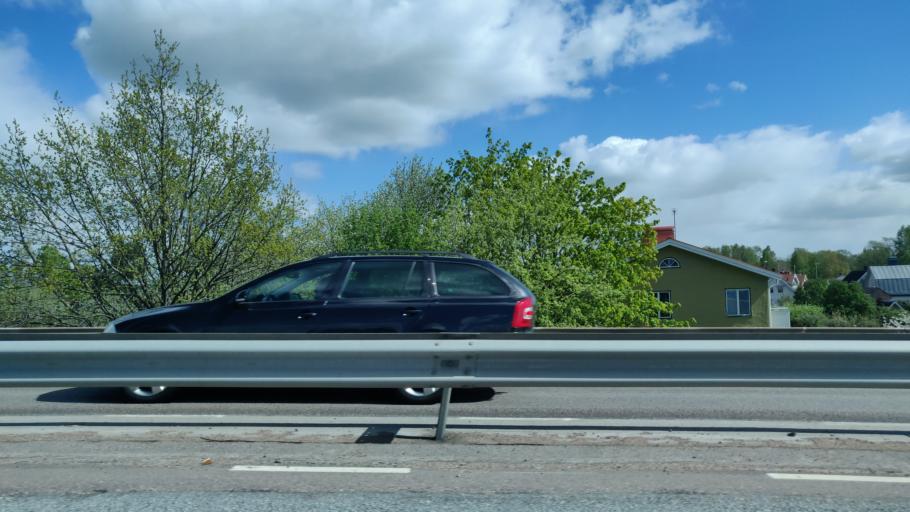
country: SE
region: Vaermland
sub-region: Karlstads Kommun
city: Karlstad
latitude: 59.3875
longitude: 13.5326
